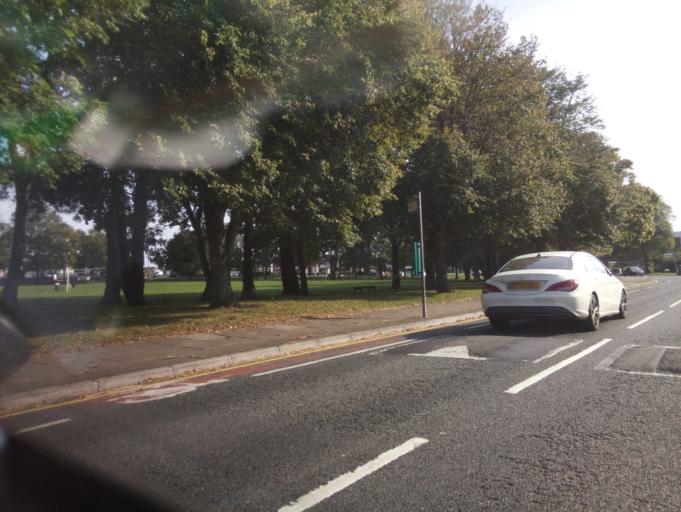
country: GB
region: Wales
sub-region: Cardiff
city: Cardiff
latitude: 51.5113
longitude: -3.1312
